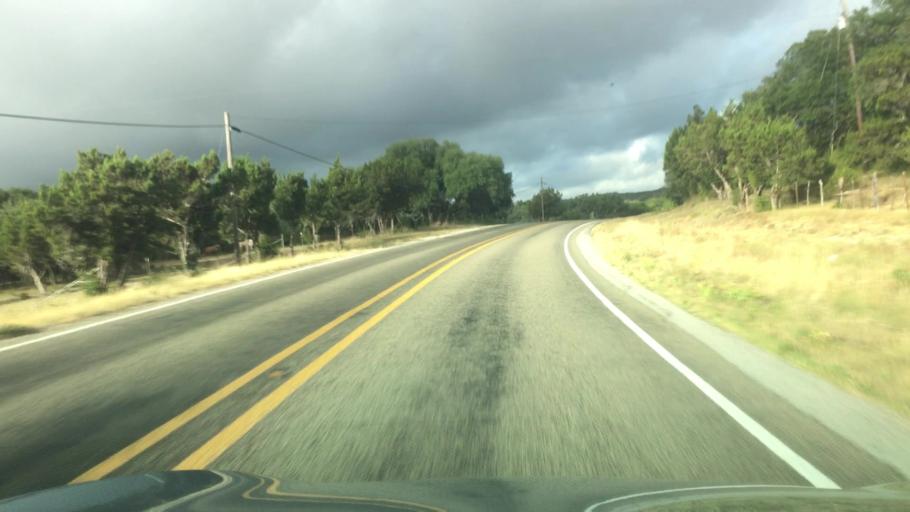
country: US
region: Texas
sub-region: Hays County
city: Dripping Springs
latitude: 30.1595
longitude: -98.2461
